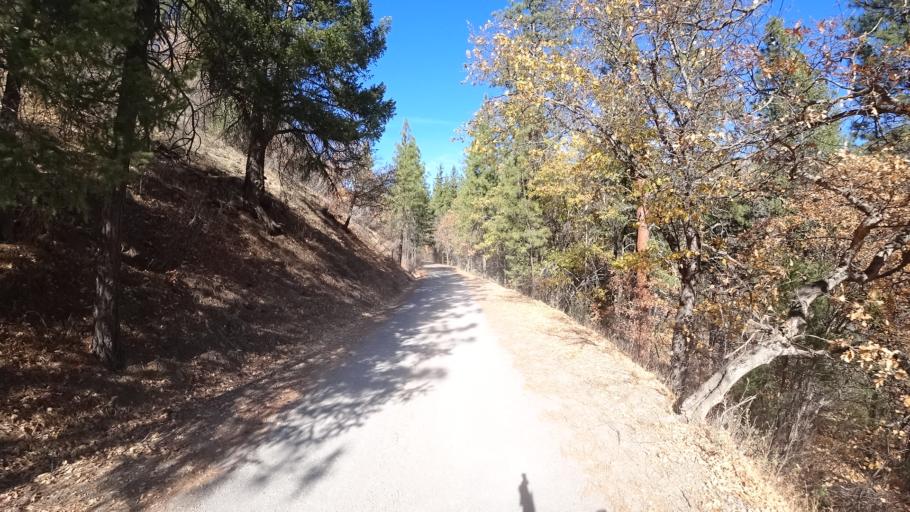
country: US
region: California
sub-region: Siskiyou County
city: Yreka
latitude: 41.8593
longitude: -122.7058
